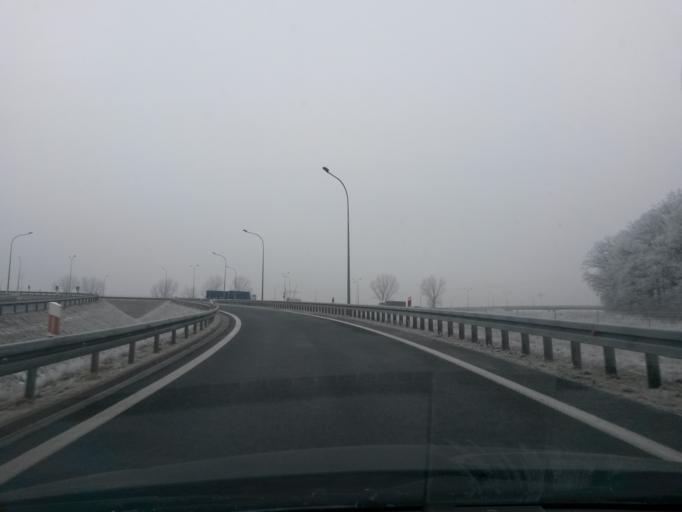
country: PL
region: Greater Poland Voivodeship
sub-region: Powiat poznanski
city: Kostrzyn
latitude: 52.3970
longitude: 17.2597
